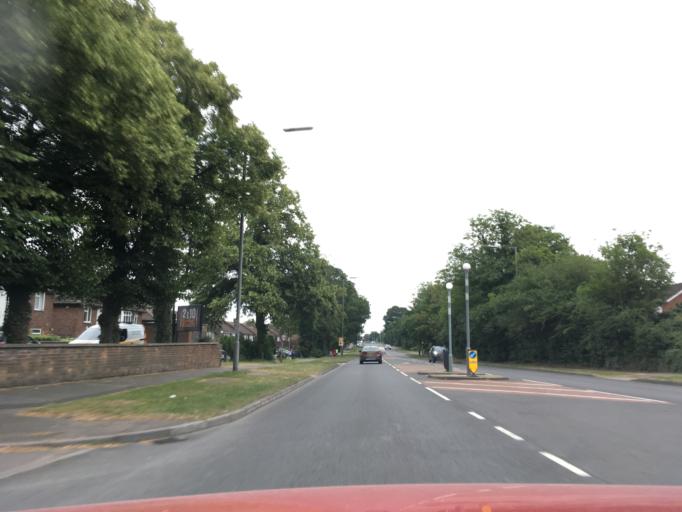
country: GB
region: England
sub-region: Central Bedfordshire
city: Dunstable
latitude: 51.8759
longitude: -0.5061
